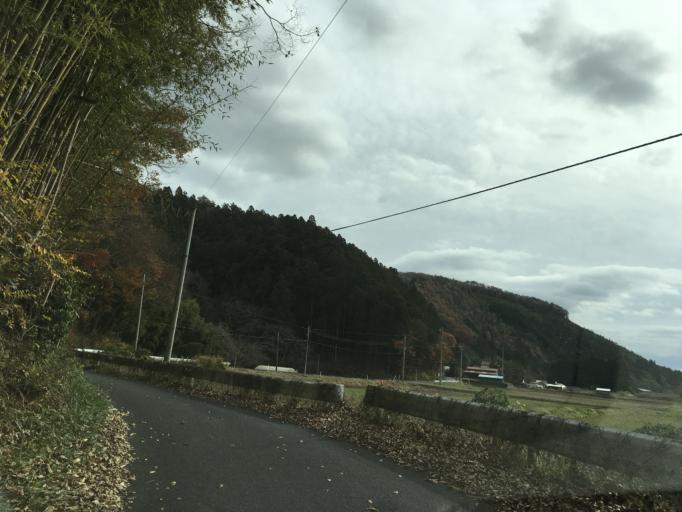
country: JP
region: Iwate
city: Ichinoseki
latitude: 38.7842
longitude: 141.2648
